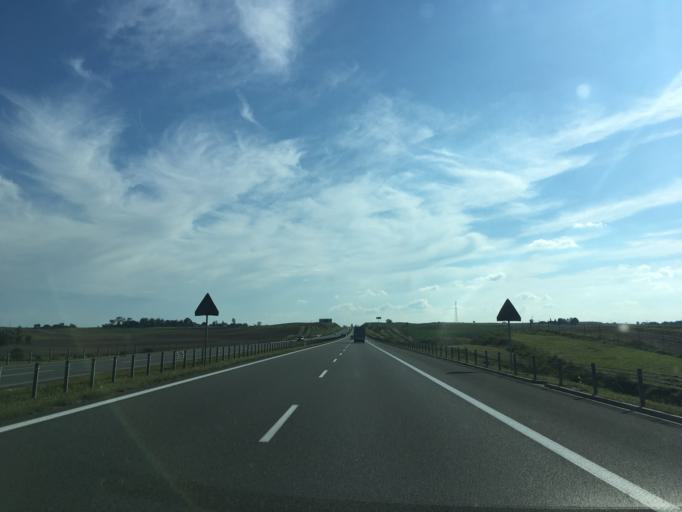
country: PL
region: Kujawsko-Pomorskie
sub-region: Powiat chelminski
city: Lisewo
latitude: 53.3323
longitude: 18.7085
